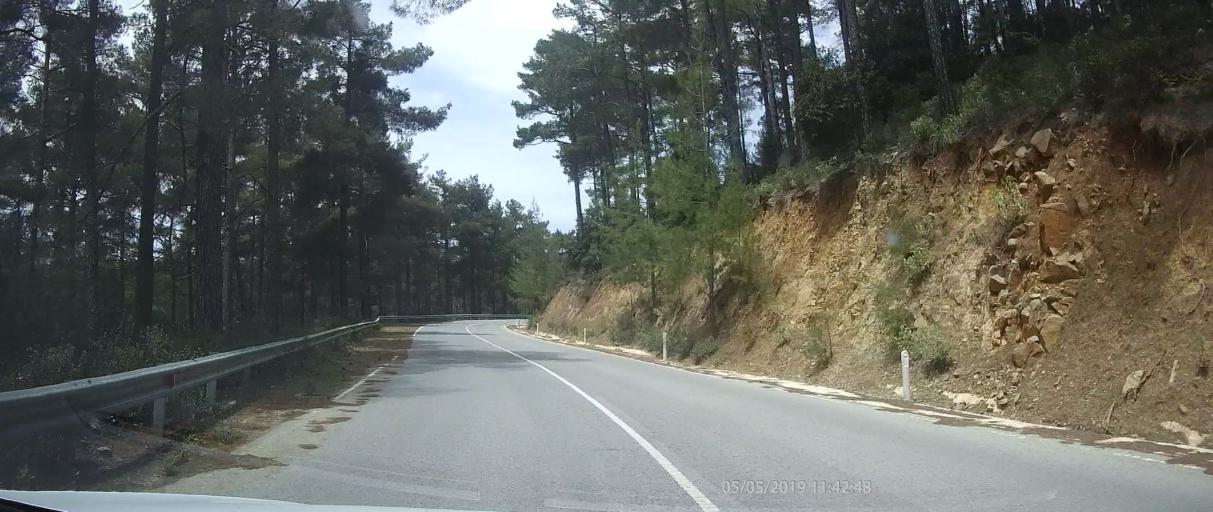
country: CY
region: Lefkosia
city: Kato Pyrgos
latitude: 35.0042
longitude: 32.6706
